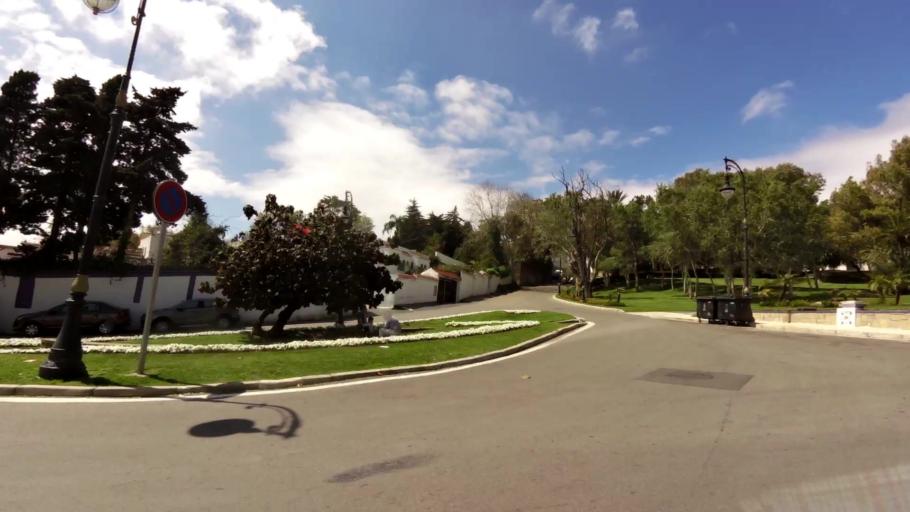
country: MA
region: Tanger-Tetouan
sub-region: Tanger-Assilah
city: Tangier
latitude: 35.7866
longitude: -5.8437
